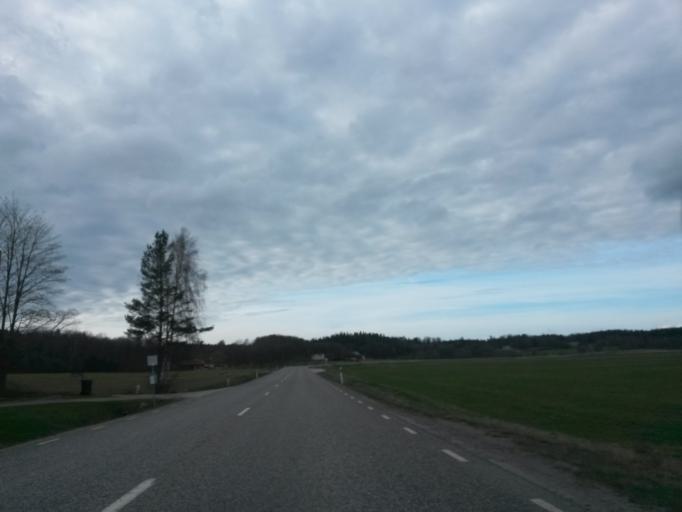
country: SE
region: Vaestra Goetaland
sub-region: Vargarda Kommun
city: Jonstorp
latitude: 58.0275
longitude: 12.6334
